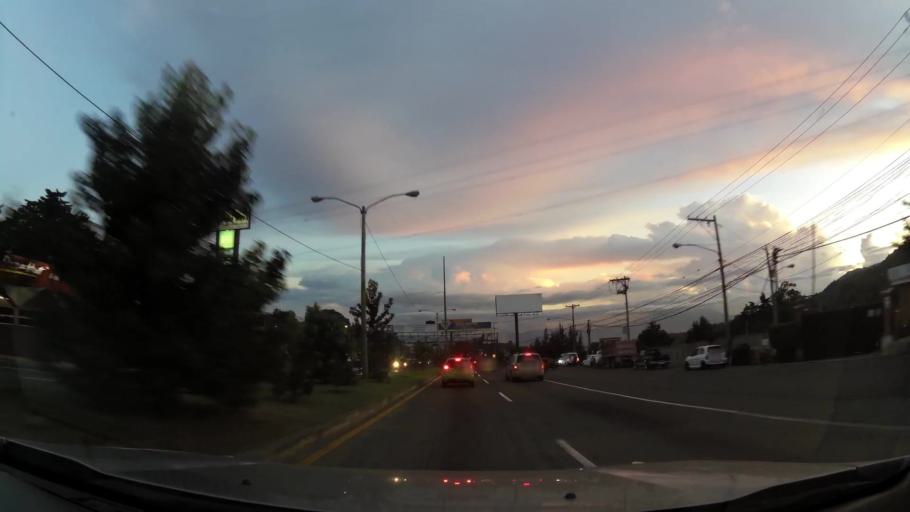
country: GT
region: Guatemala
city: Mixco
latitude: 14.6181
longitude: -90.6110
